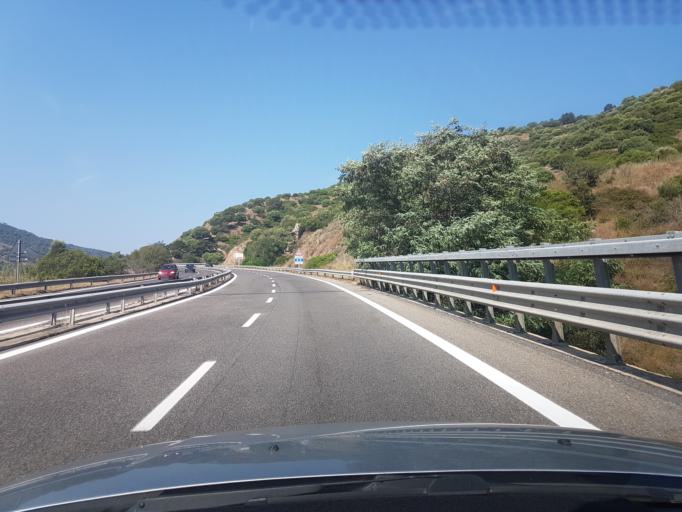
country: IT
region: Sardinia
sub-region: Provincia di Nuoro
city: Nuoro
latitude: 40.3478
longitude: 9.3296
